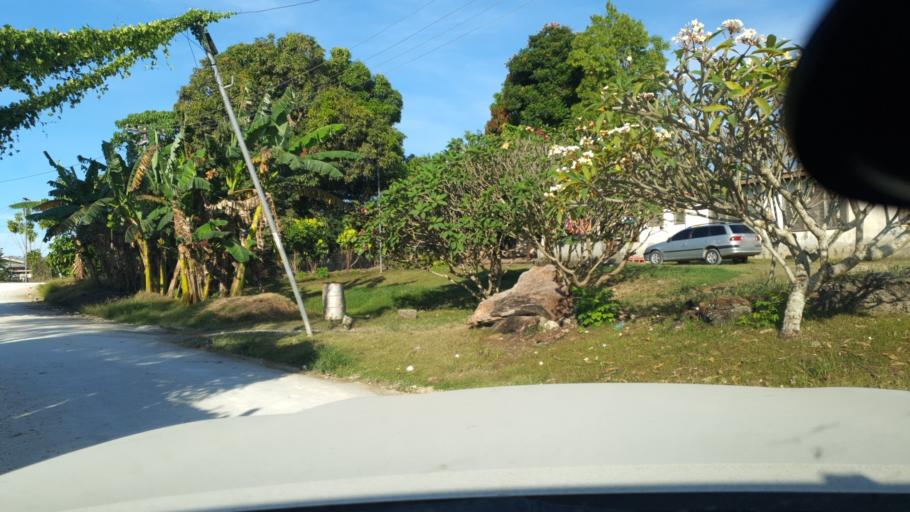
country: SB
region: Guadalcanal
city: Honiara
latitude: -9.4306
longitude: 160.0025
